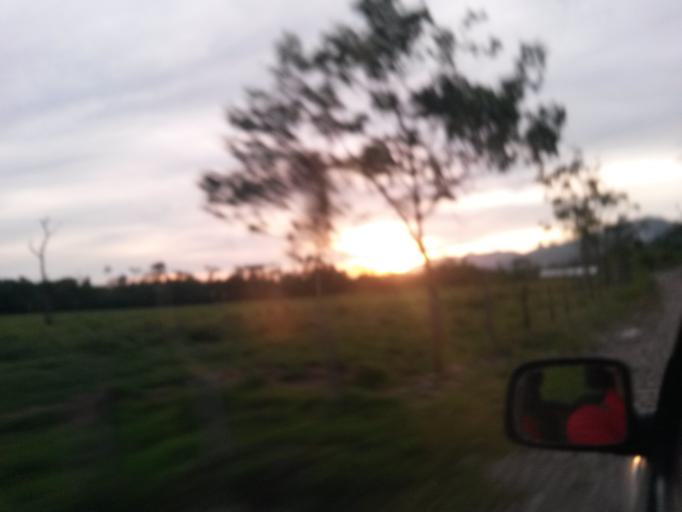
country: CO
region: Putumayo
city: Puerto Guzman
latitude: 1.1345
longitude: -76.2689
